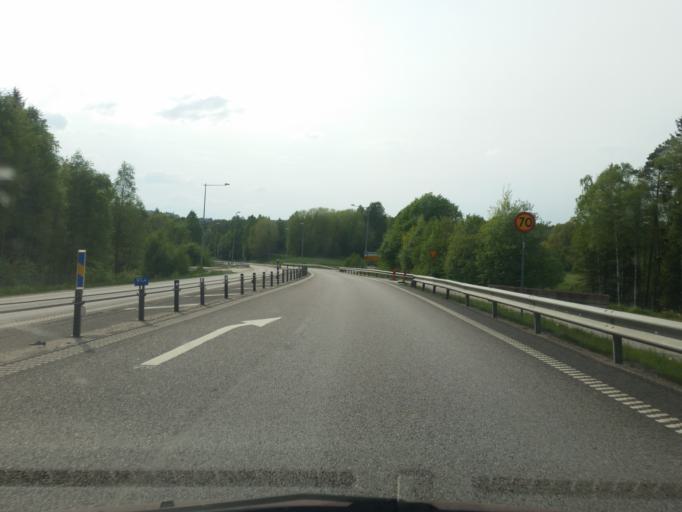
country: SE
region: Vaestra Goetaland
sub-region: Ulricehamns Kommun
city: Ulricehamn
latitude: 57.8027
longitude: 13.3768
